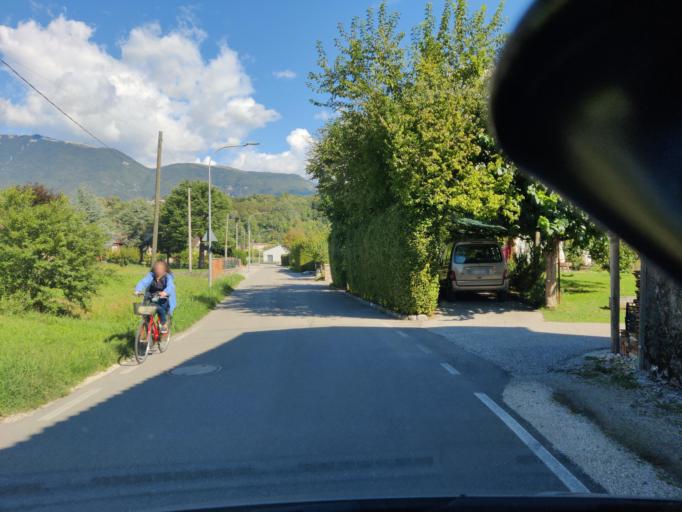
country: IT
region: Veneto
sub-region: Provincia di Treviso
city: Cappella Maggiore
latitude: 45.9763
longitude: 12.3351
